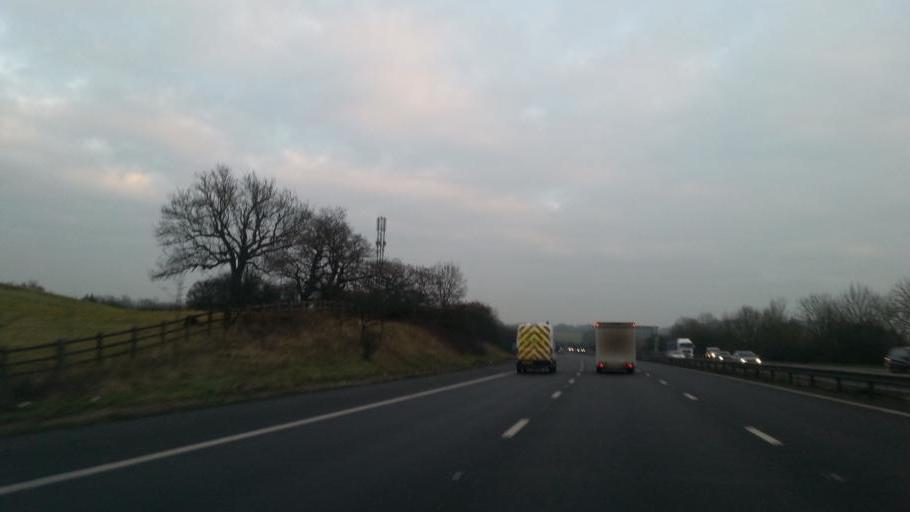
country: GB
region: England
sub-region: Worcestershire
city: Alvechurch
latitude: 52.3549
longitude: -1.9195
